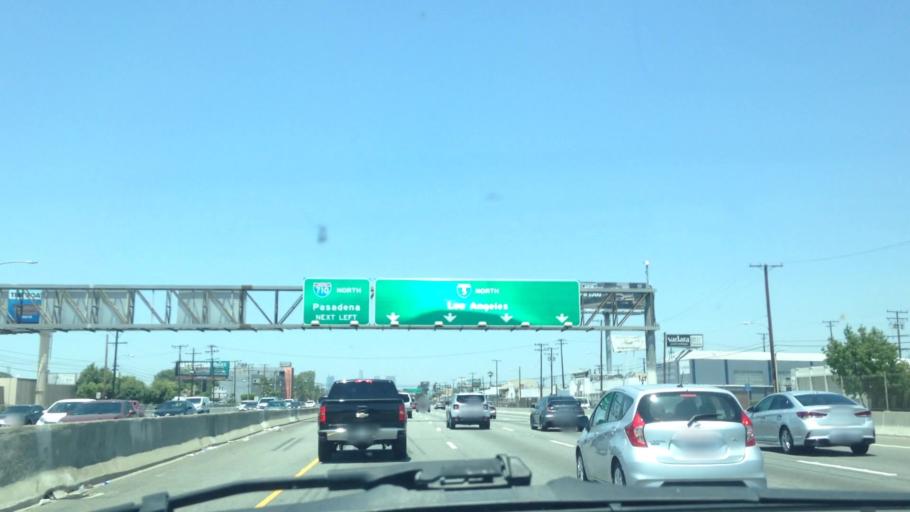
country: US
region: California
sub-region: Los Angeles County
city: Commerce
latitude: 34.0119
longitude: -118.1622
